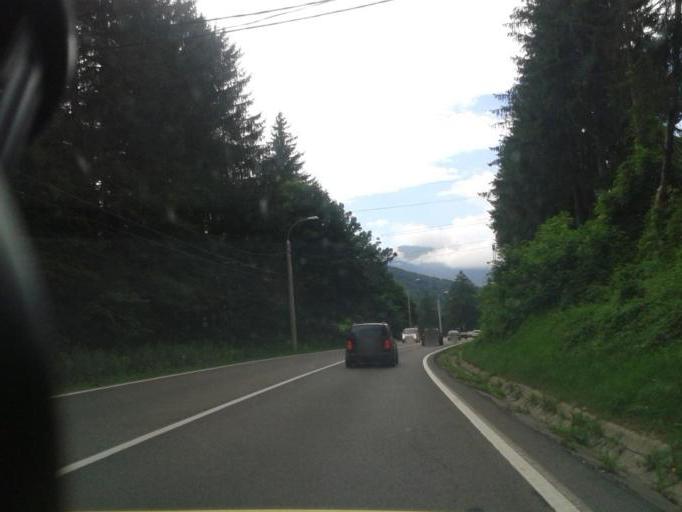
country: RO
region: Prahova
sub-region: Oras Sinaia
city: Sinaia
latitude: 45.3111
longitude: 25.5704
